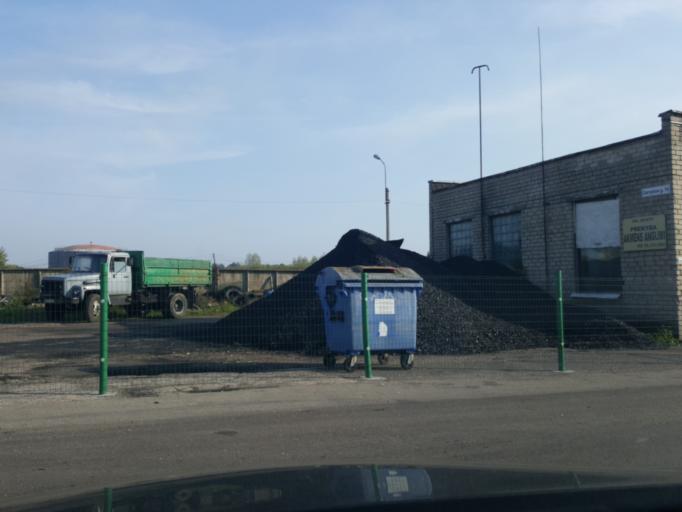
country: LT
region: Alytaus apskritis
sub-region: Alytus
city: Alytus
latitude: 54.4373
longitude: 24.0239
